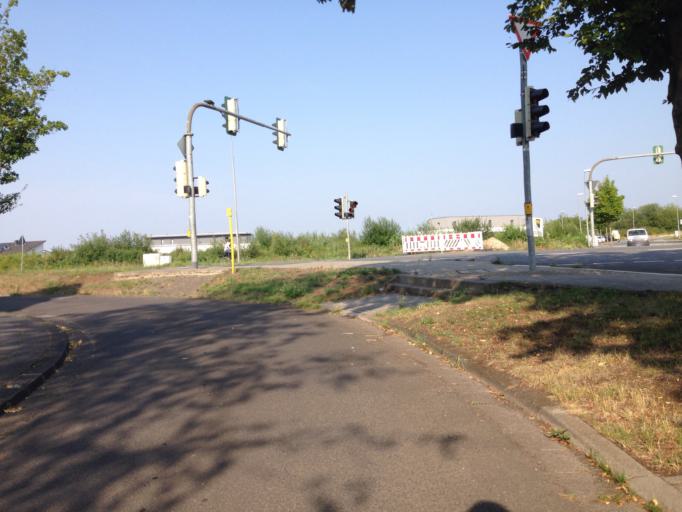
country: DE
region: Hesse
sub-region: Regierungsbezirk Giessen
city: Giessen
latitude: 50.6107
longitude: 8.7018
